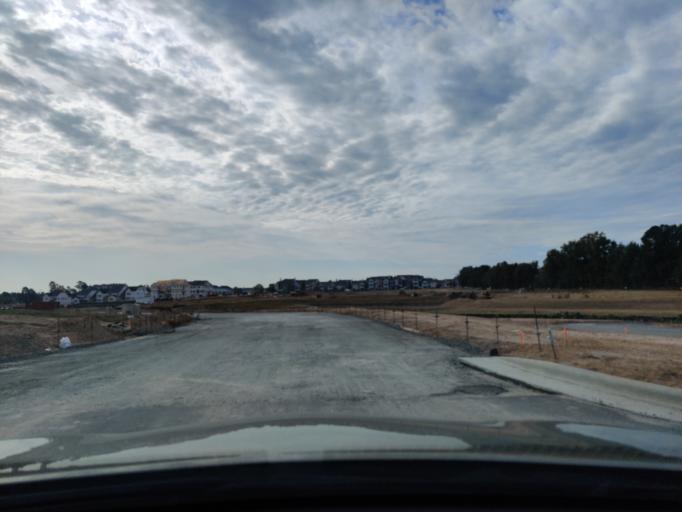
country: US
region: North Carolina
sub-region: Wake County
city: Morrisville
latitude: 35.8272
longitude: -78.8577
